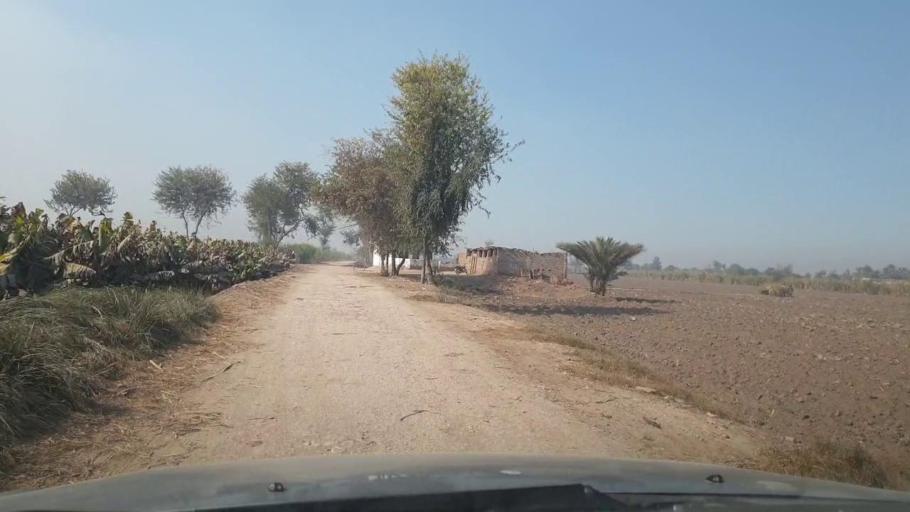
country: PK
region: Sindh
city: Ghotki
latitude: 28.0280
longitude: 69.2523
